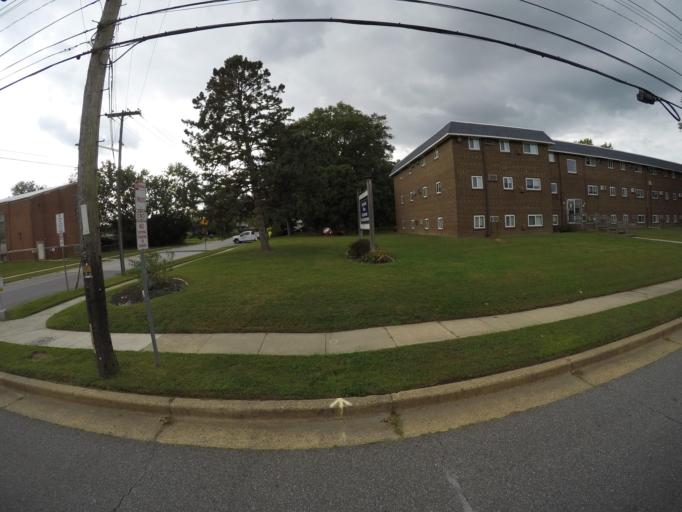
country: US
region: Delaware
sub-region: New Castle County
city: Brookside
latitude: 39.6671
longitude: -75.7272
